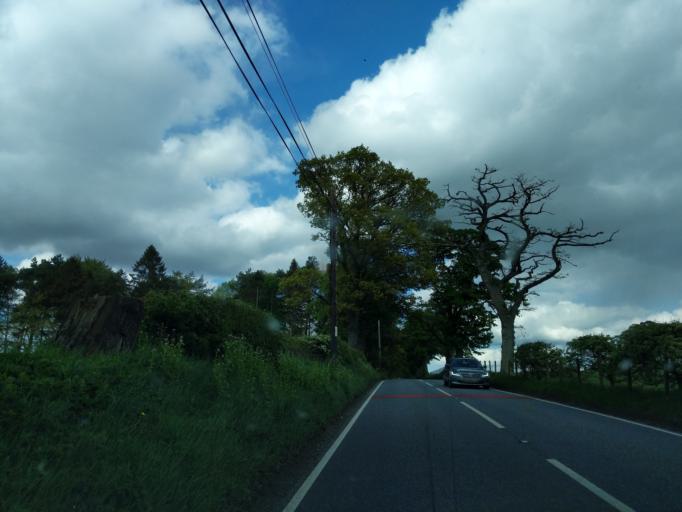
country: GB
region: Scotland
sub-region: Stirling
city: Callander
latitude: 56.1284
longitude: -4.2272
